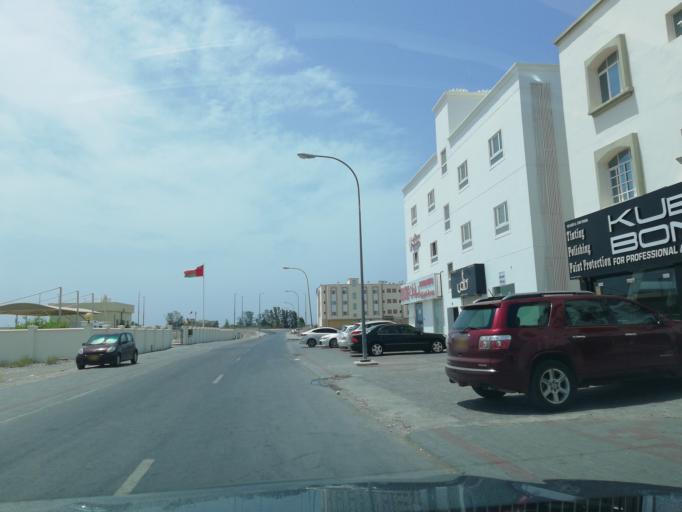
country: OM
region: Muhafazat Masqat
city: As Sib al Jadidah
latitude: 23.6627
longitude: 58.1937
